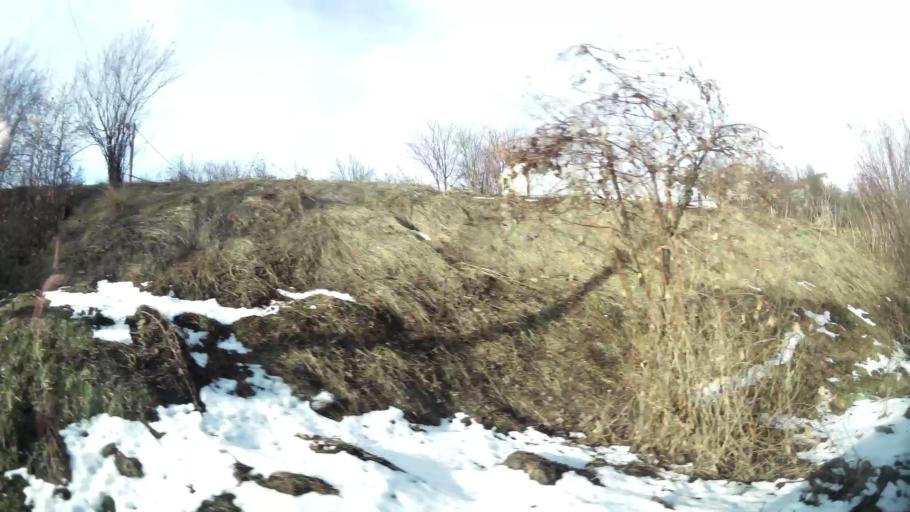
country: RS
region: Central Serbia
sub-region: Belgrade
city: Rakovica
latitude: 44.7206
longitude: 20.4329
